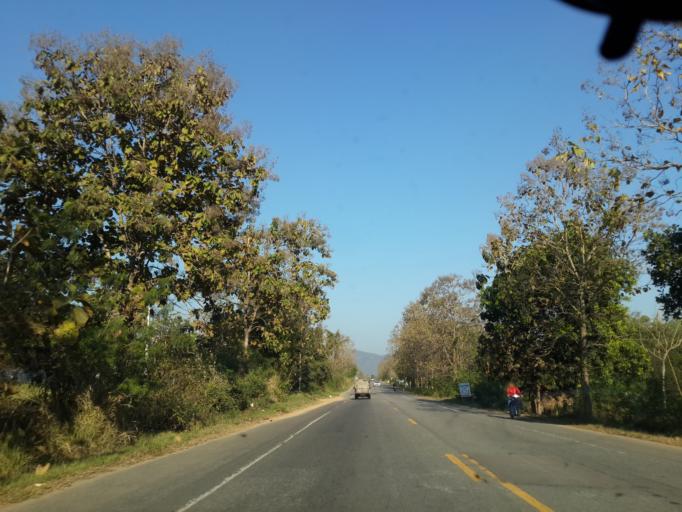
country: TH
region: Chiang Mai
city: Mae On
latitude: 18.7490
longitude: 99.2181
